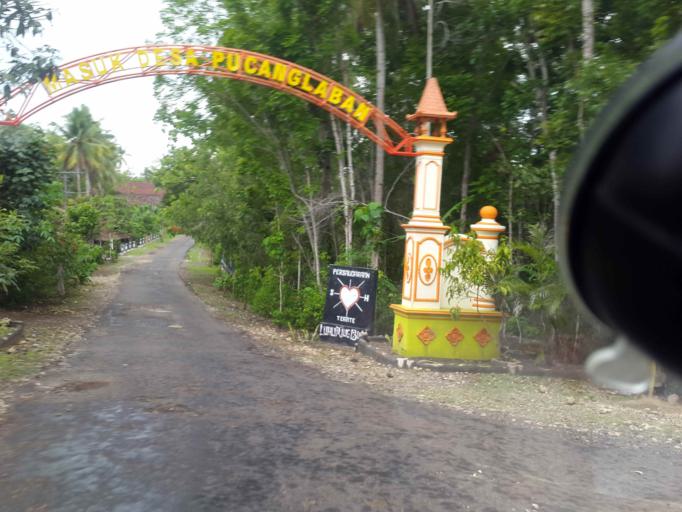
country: ID
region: East Java
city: Kalidawe
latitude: -8.2508
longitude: 112.0149
